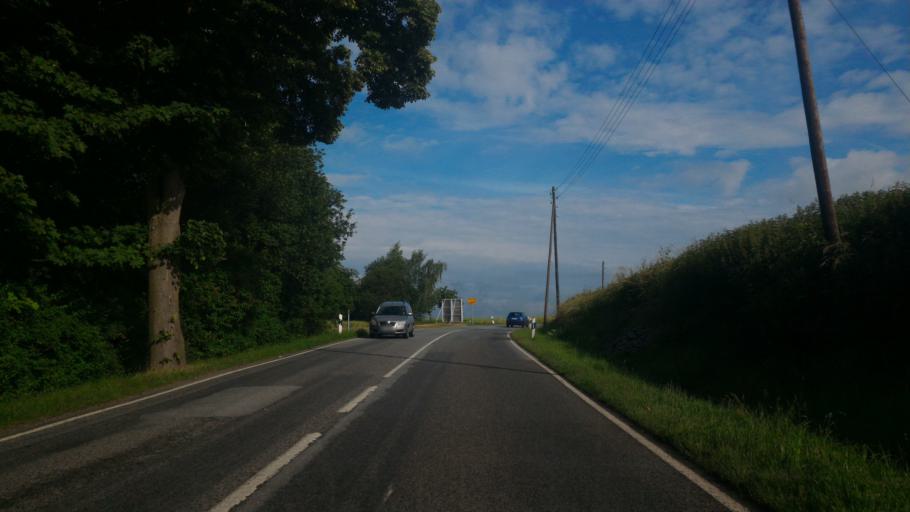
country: DE
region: Saxony
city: Mittelherwigsdorf
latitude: 50.9080
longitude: 14.7652
